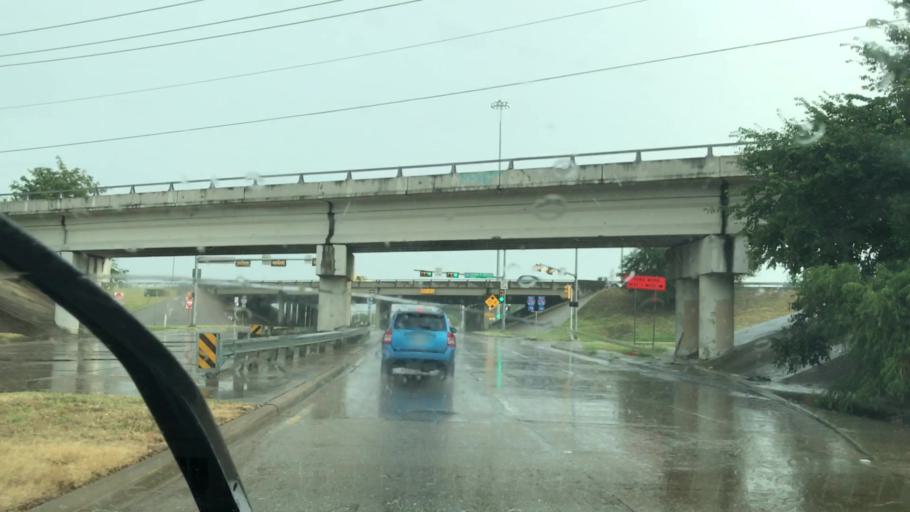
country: US
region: Texas
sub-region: Dallas County
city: Garland
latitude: 32.8870
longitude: -96.7004
